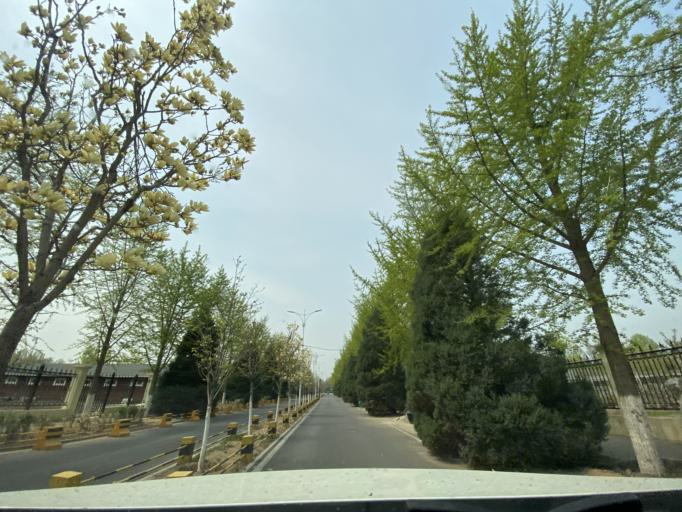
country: CN
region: Beijing
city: Sijiqing
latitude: 39.9430
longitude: 116.2436
